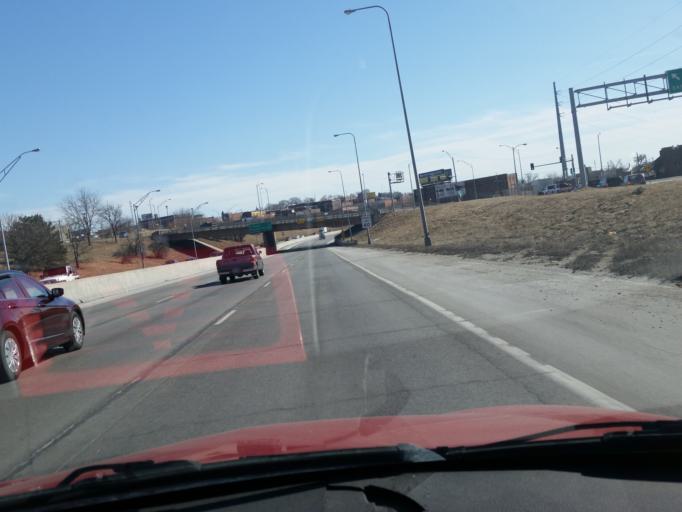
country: US
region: Nebraska
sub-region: Douglas County
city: Omaha
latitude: 41.2138
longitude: -95.9520
